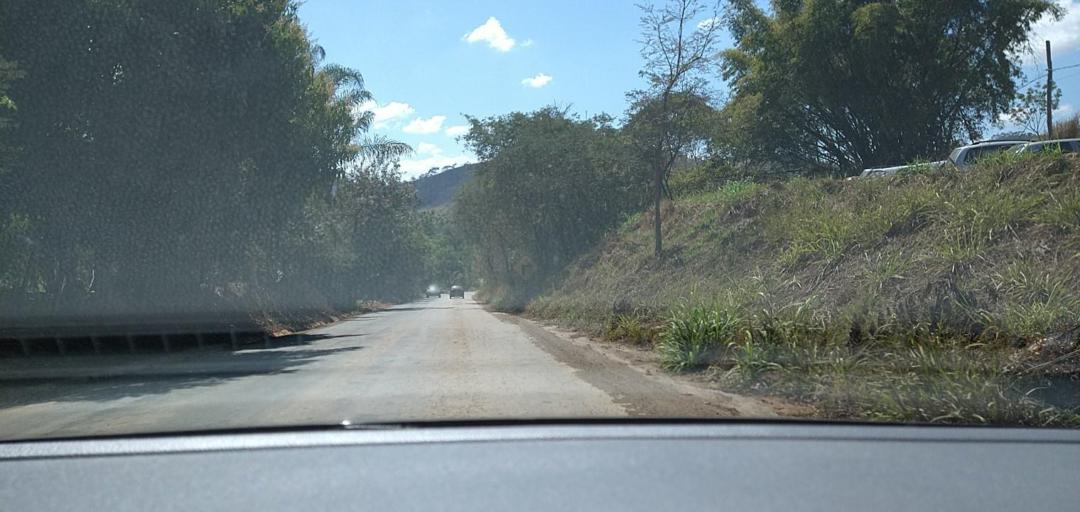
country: BR
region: Minas Gerais
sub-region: Ponte Nova
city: Ponte Nova
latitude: -20.2582
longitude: -42.8877
